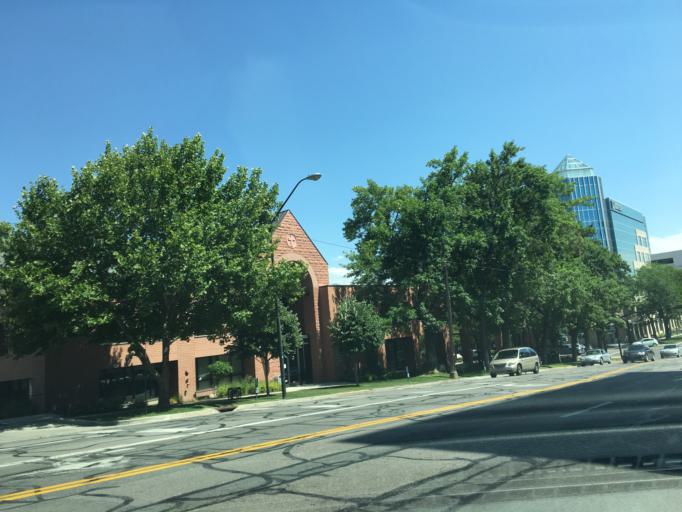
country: US
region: Utah
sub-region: Salt Lake County
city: Salt Lake City
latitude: 40.7682
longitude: -111.8855
